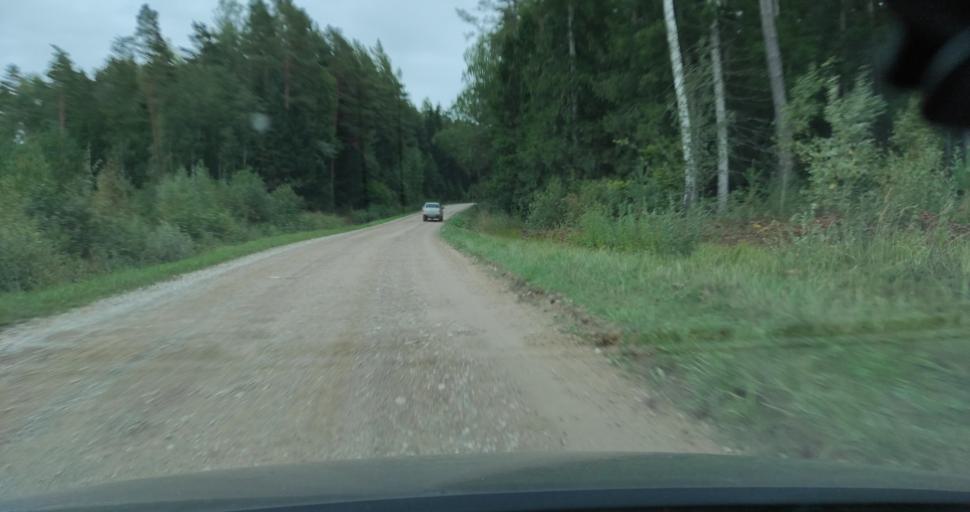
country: LV
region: Talsu Rajons
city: Stende
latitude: 57.0369
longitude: 22.3173
